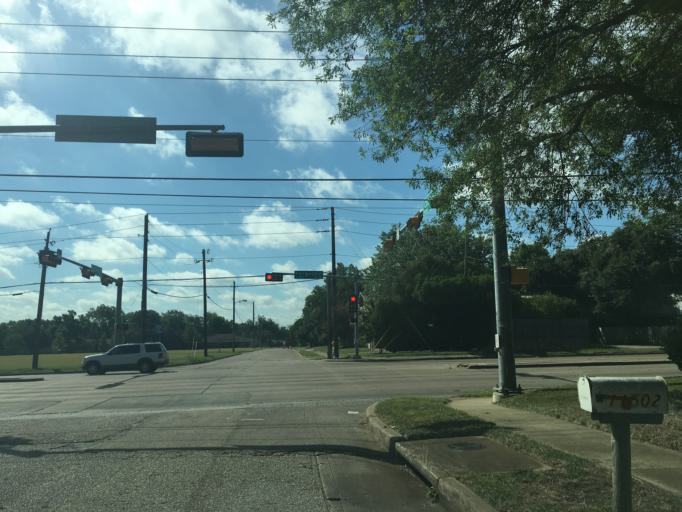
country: US
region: Texas
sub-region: Dallas County
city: Garland
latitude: 32.8509
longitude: -96.6552
